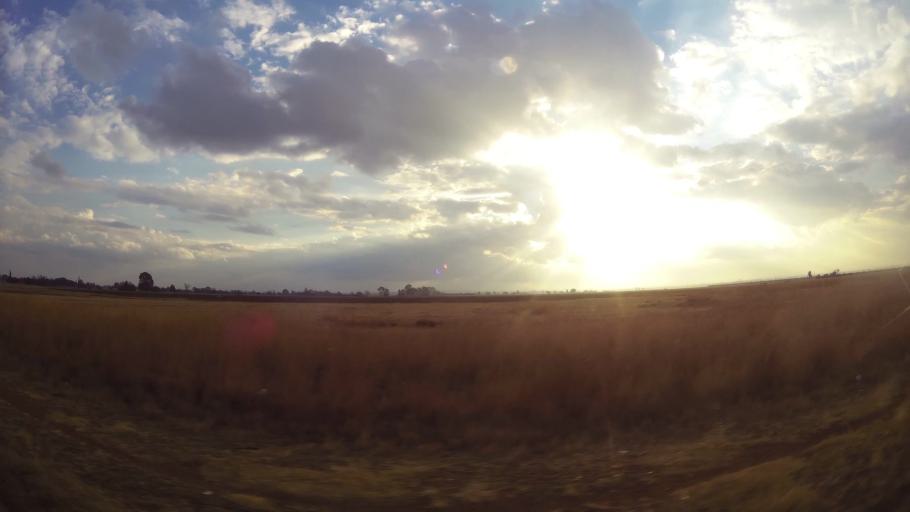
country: ZA
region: Gauteng
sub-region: Sedibeng District Municipality
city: Vanderbijlpark
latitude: -26.6253
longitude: 27.8106
